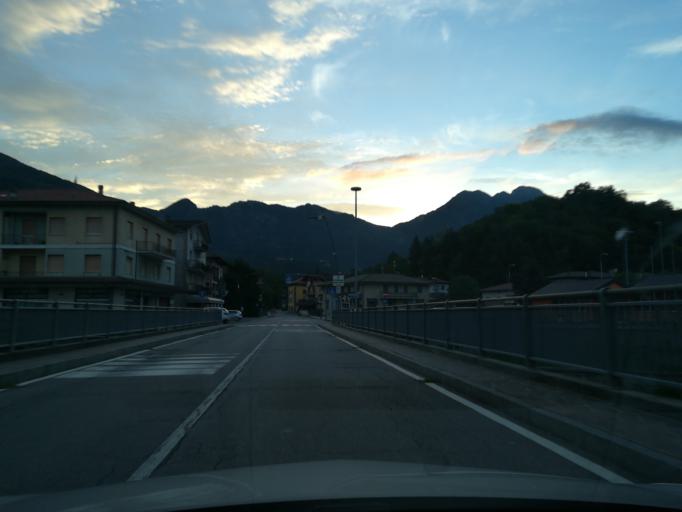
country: IT
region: Lombardy
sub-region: Provincia di Bergamo
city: Selino Basso
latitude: 45.8150
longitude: 9.5324
